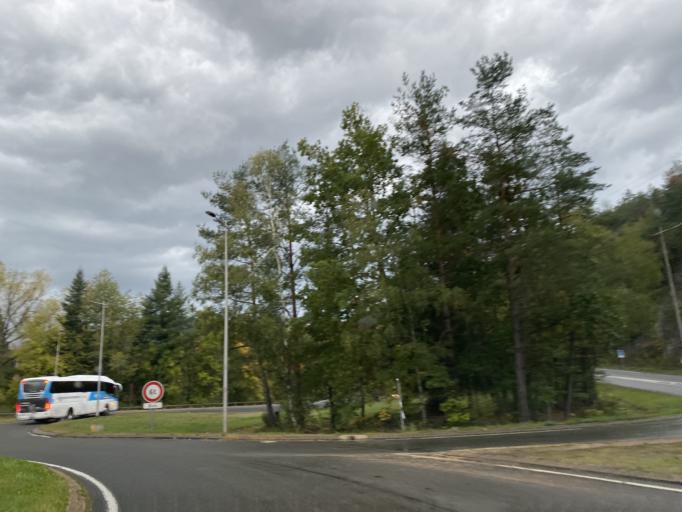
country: FR
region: Auvergne
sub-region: Departement du Puy-de-Dome
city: Celles-sur-Durolle
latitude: 45.8666
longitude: 3.6250
